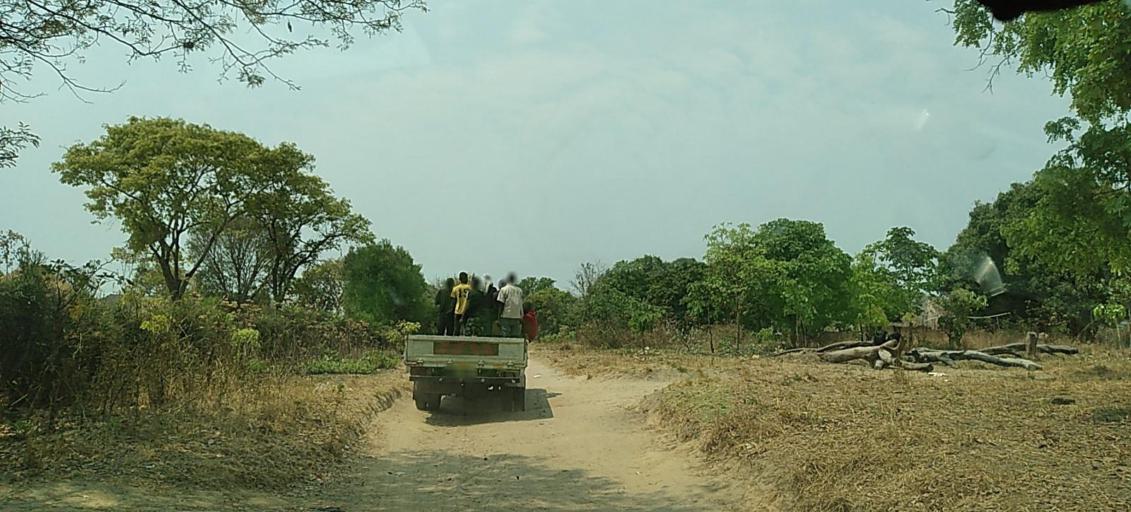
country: ZM
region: North-Western
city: Kabompo
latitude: -13.4847
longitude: 24.4608
